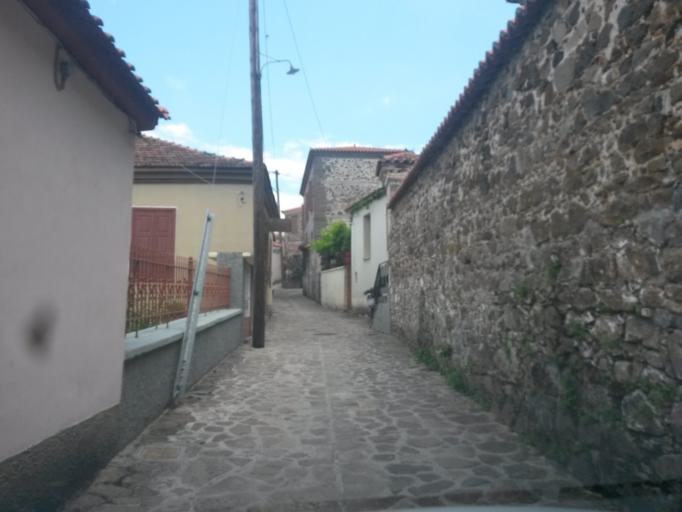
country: GR
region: North Aegean
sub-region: Nomos Lesvou
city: Eresos
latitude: 39.2258
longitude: 26.0513
